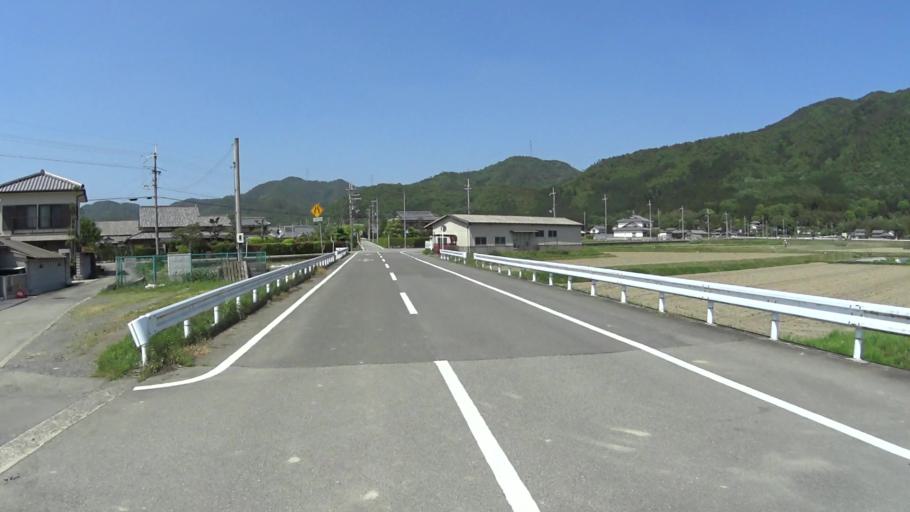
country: JP
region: Kyoto
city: Kameoka
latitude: 35.0729
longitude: 135.5621
